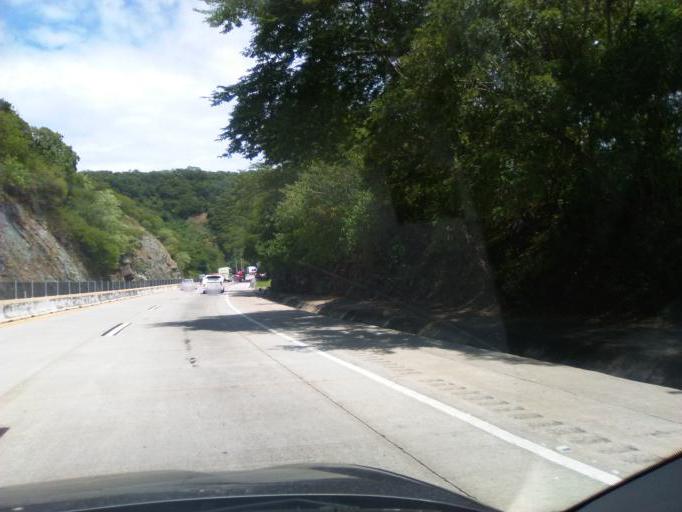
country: MX
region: Guerrero
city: Tierra Colorada
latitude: 17.1091
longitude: -99.5797
